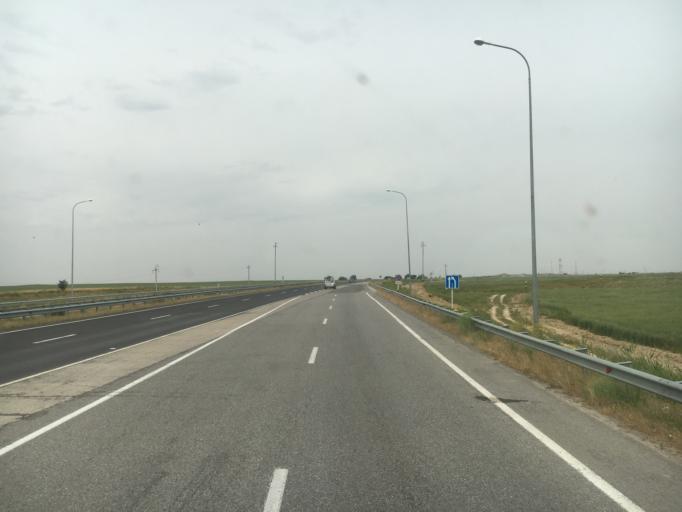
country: KZ
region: Ongtustik Qazaqstan
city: Temirlanovka
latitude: 42.5305
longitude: 69.3419
